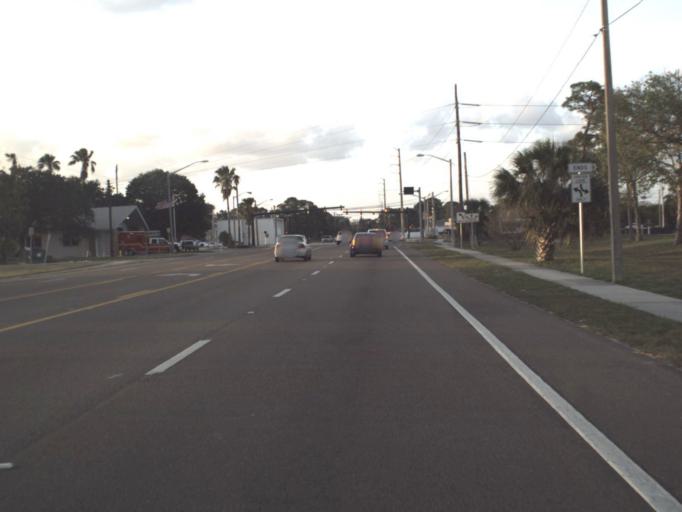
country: US
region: Florida
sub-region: Brevard County
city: Rockledge
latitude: 28.3539
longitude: -80.7425
